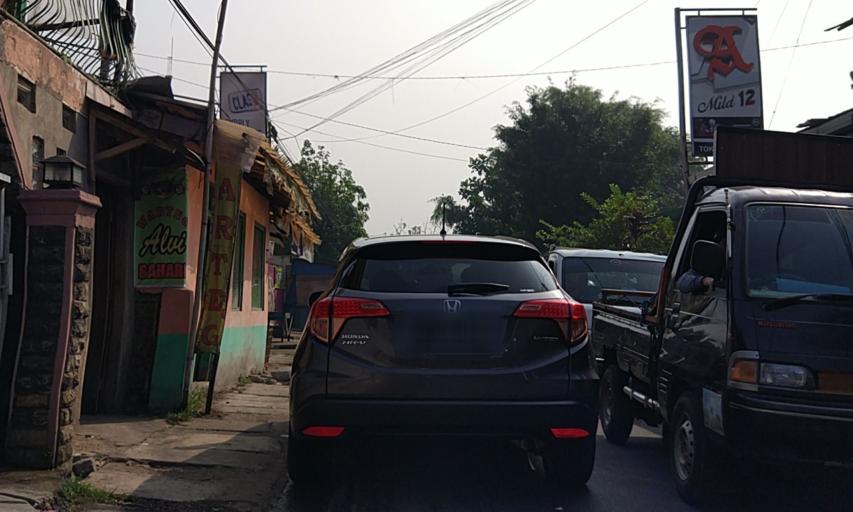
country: ID
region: West Java
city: Bandung
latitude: -6.9047
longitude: 107.6490
